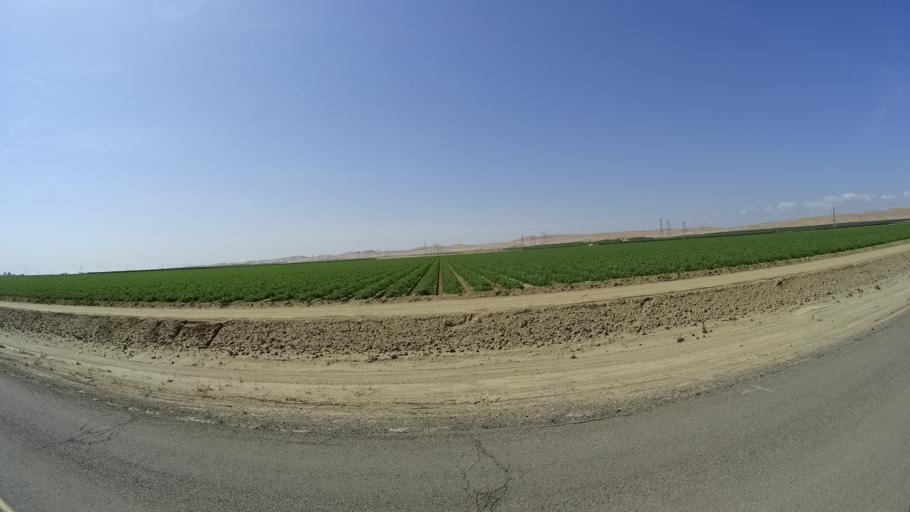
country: US
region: California
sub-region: Kings County
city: Avenal
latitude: 36.0726
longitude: -120.0544
